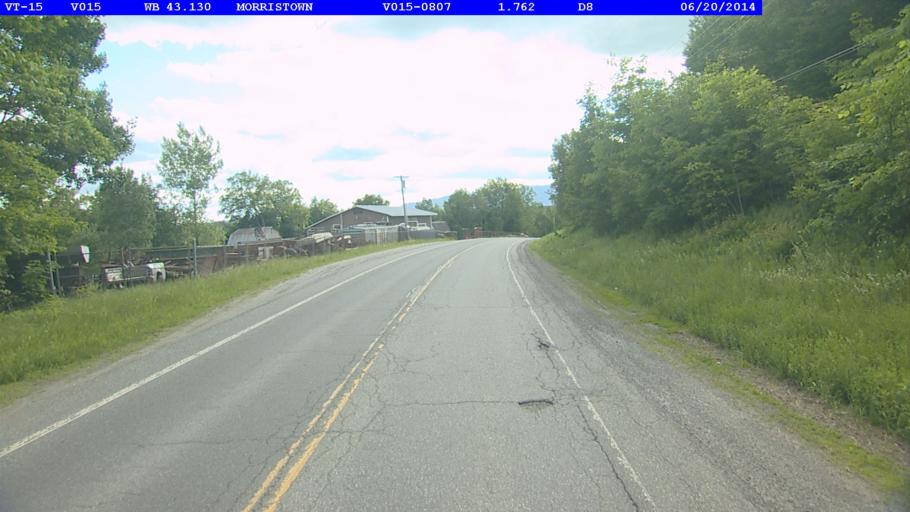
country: US
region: Vermont
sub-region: Lamoille County
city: Morrisville
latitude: 44.5681
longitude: -72.5789
